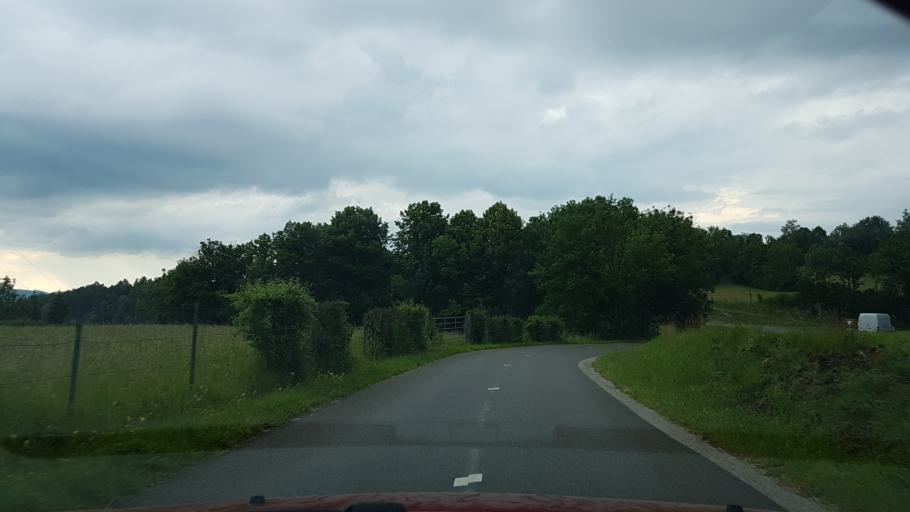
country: FR
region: Franche-Comte
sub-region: Departement du Jura
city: Clairvaux-les-Lacs
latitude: 46.5456
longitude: 5.7476
